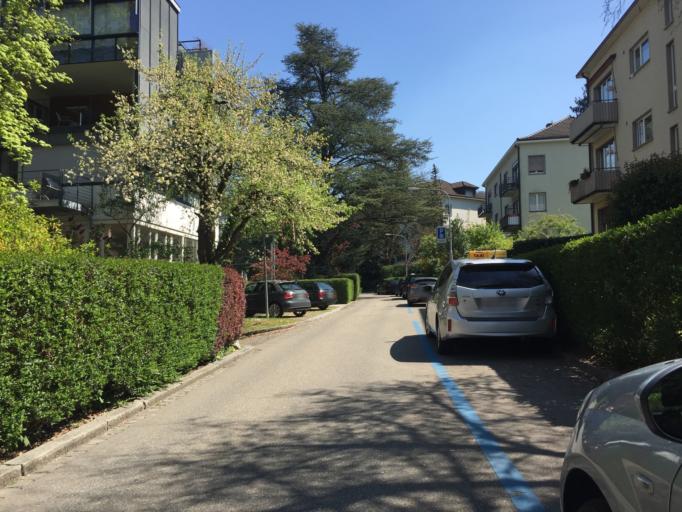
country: CH
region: Zurich
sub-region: Bezirk Zuerich
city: Zuerich (Kreis 11) / Oerlikon
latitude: 47.4021
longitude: 8.5493
